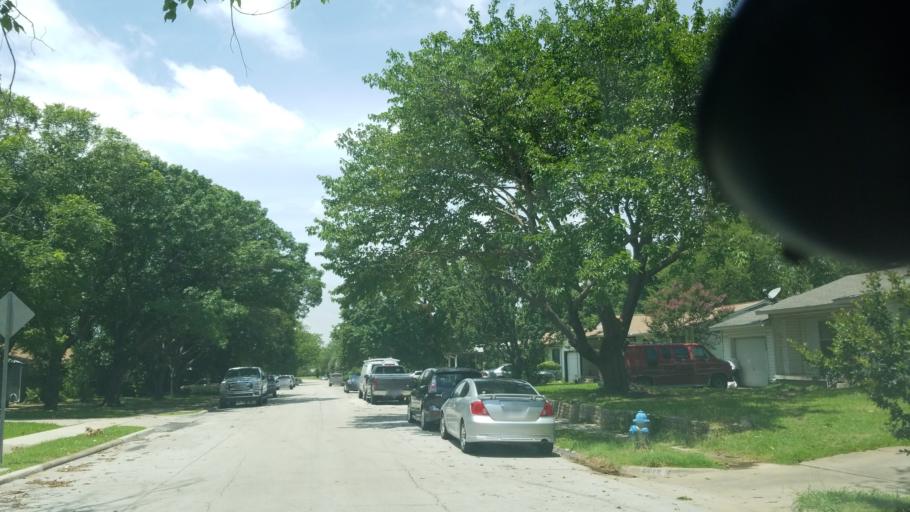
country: US
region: Texas
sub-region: Dallas County
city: Irving
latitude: 32.8479
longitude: -96.9745
